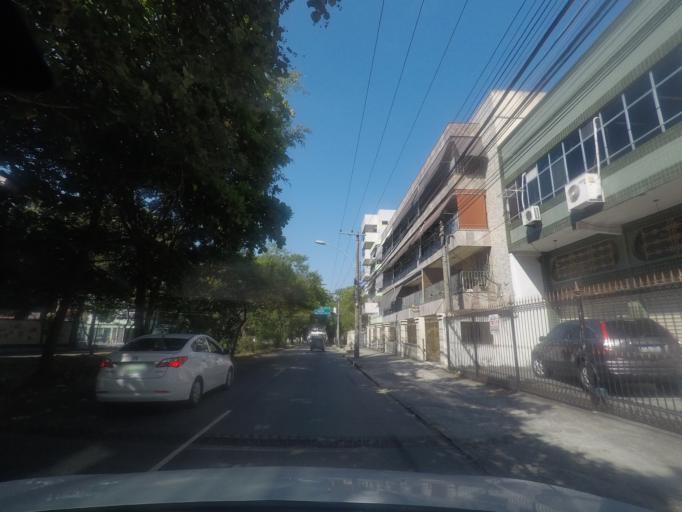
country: BR
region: Rio de Janeiro
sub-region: Sao Joao De Meriti
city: Sao Joao de Meriti
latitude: -22.8825
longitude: -43.3716
